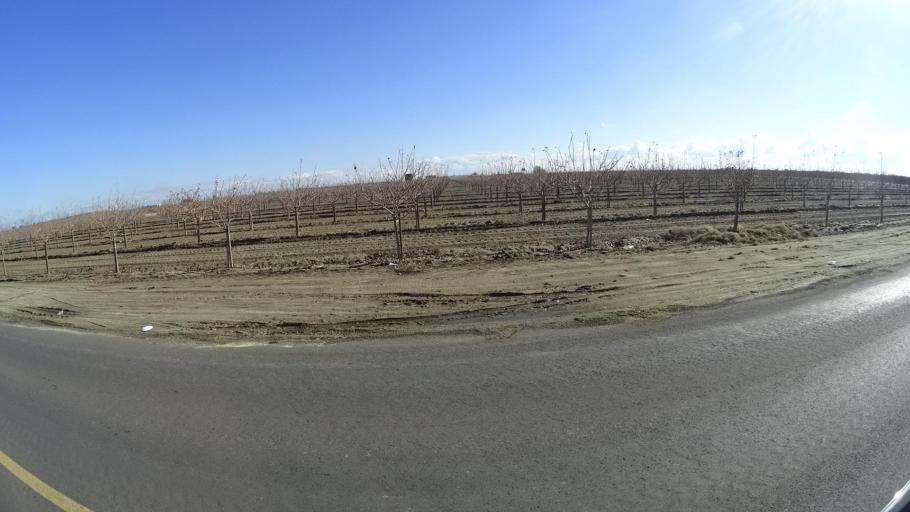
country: US
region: California
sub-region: Kern County
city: Delano
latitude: 35.7337
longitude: -119.2584
